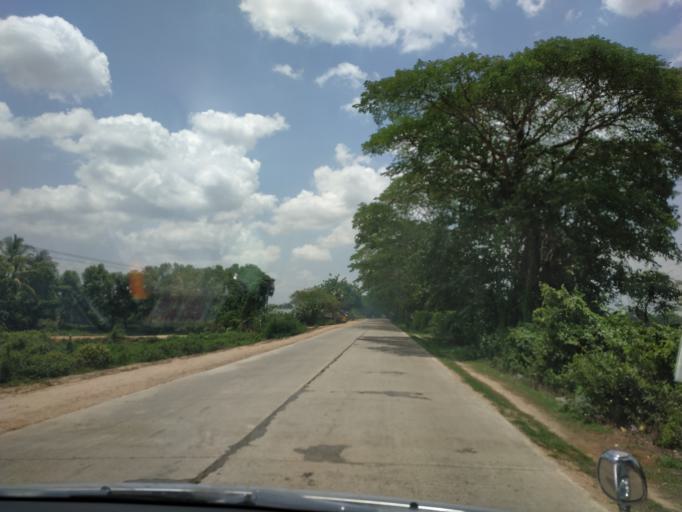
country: MM
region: Bago
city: Bago
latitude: 17.4772
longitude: 96.5059
